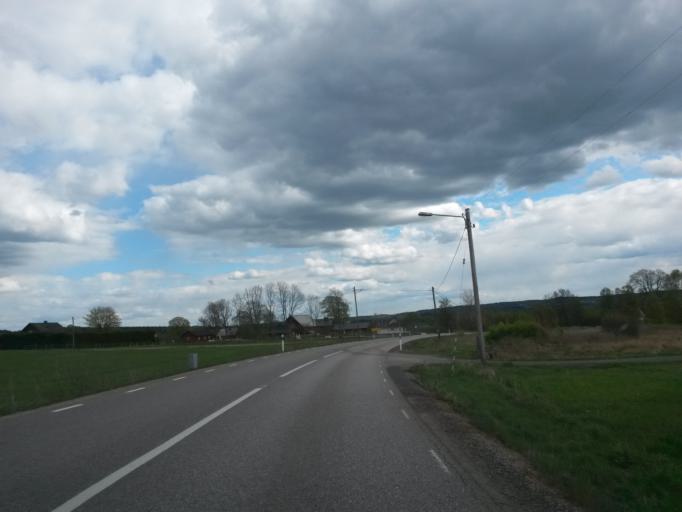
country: SE
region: Vaestra Goetaland
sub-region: Boras Kommun
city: Boras
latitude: 57.8359
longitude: 12.9894
